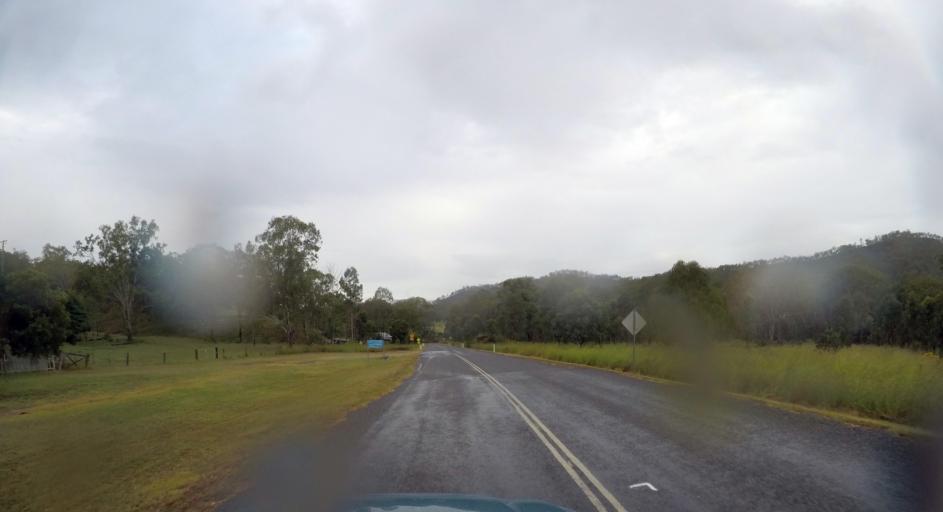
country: AU
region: Queensland
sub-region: Gladstone
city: Toolooa
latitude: -24.5455
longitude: 151.3662
